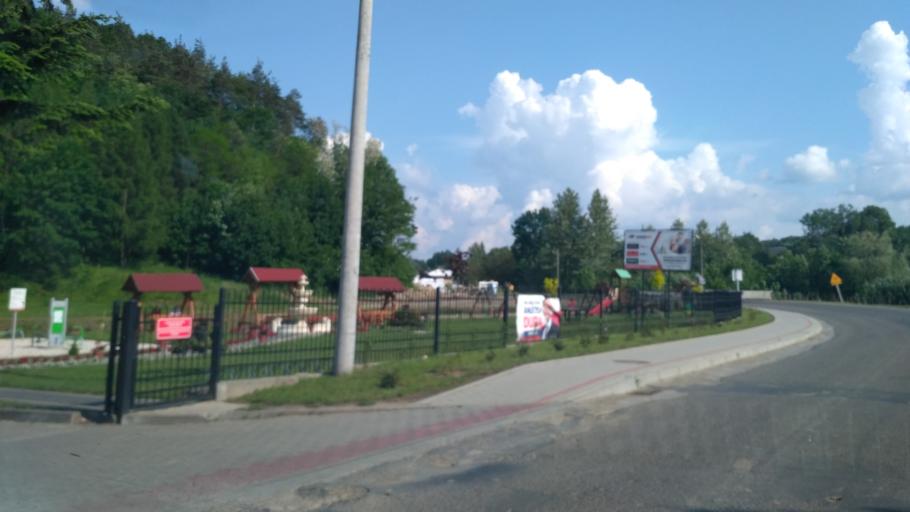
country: PL
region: Subcarpathian Voivodeship
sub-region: Powiat jaroslawski
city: Kramarzowka
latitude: 49.8855
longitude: 22.4969
